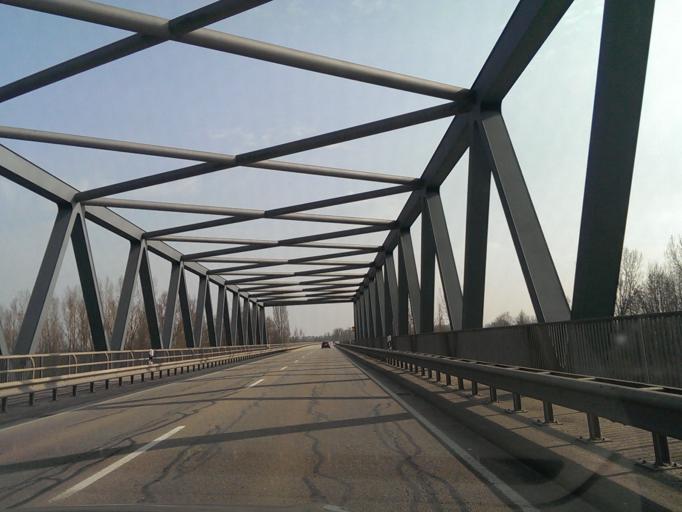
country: DE
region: Bavaria
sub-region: Upper Palatinate
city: Donaustauf
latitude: 49.0252
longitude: 12.2113
